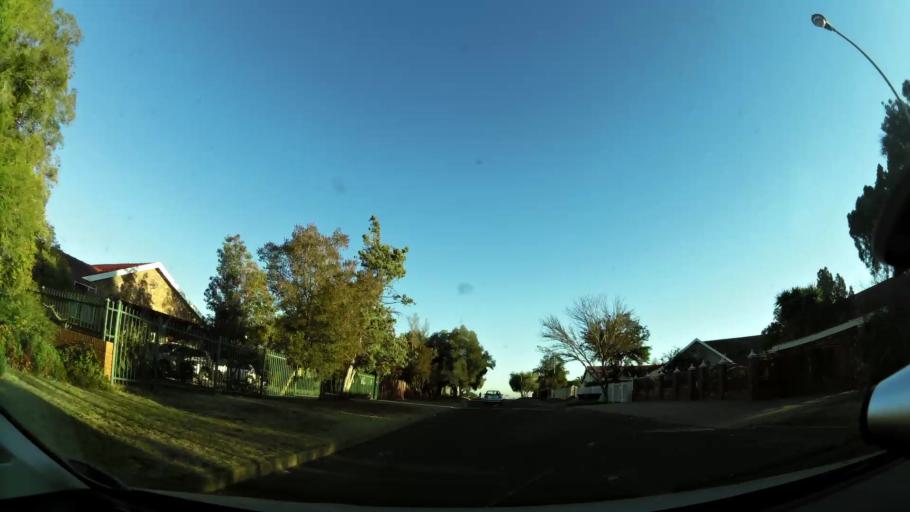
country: ZA
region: Northern Cape
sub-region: Frances Baard District Municipality
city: Kimberley
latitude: -28.7574
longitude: 24.7334
